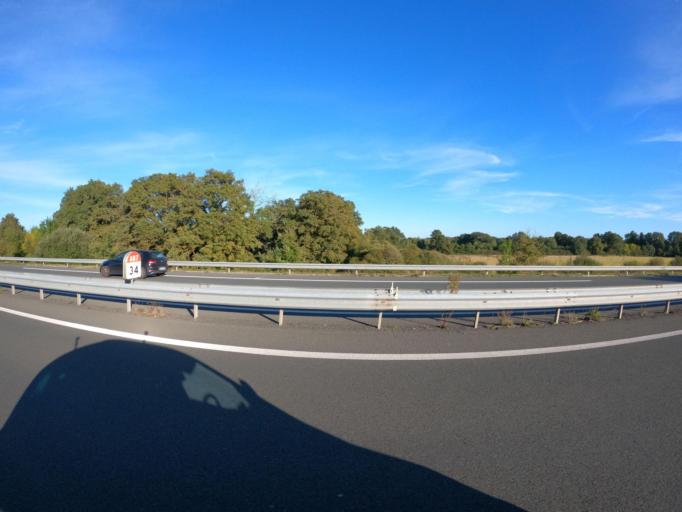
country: FR
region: Pays de la Loire
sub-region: Departement de Maine-et-Loire
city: Chemille-Melay
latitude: 47.1947
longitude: -0.7746
